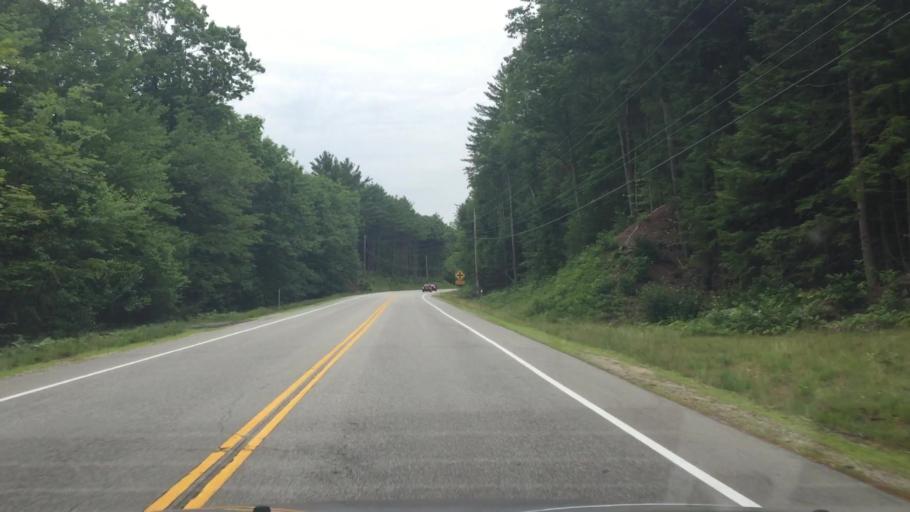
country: US
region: New Hampshire
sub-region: Carroll County
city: Sandwich
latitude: 43.7952
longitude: -71.3721
